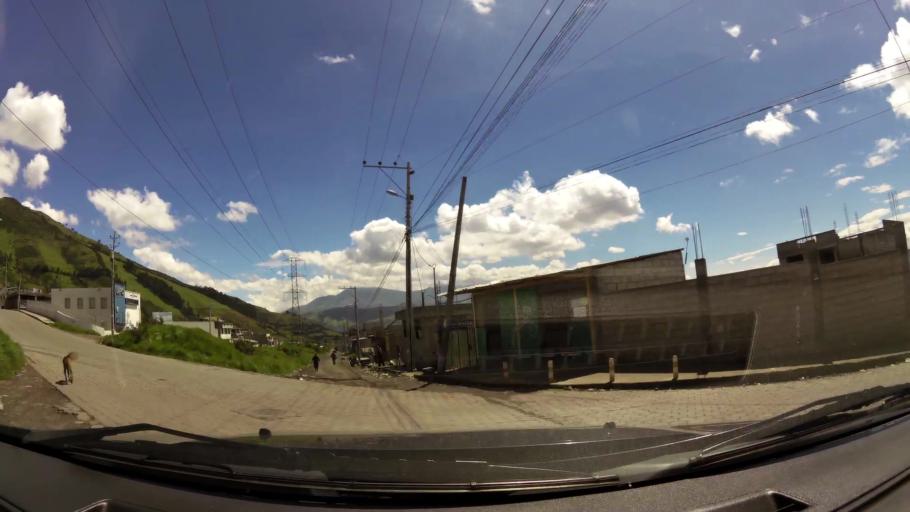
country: EC
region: Pichincha
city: Quito
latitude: -0.3271
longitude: -78.5685
